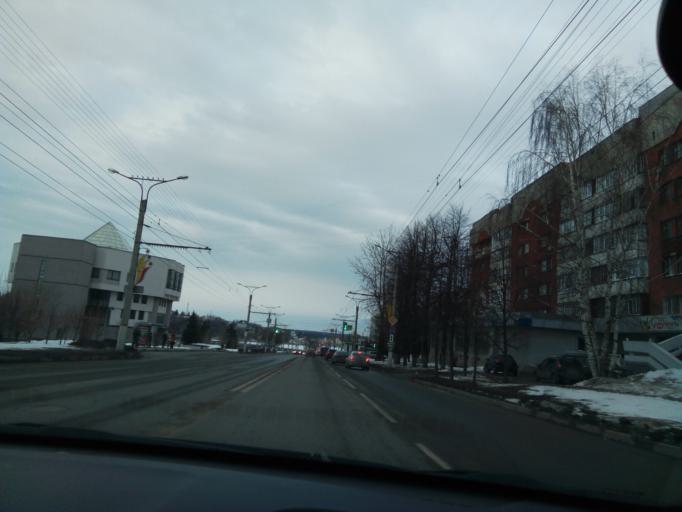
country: RU
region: Chuvashia
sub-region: Cheboksarskiy Rayon
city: Cheboksary
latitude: 56.1414
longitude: 47.2448
